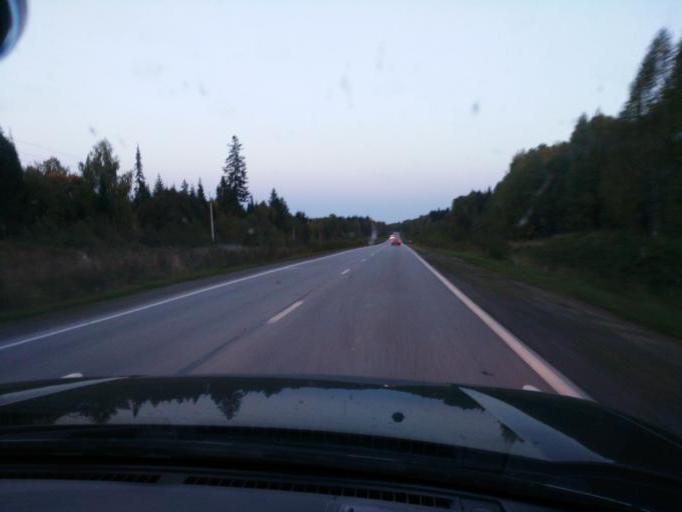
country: RU
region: Perm
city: Verkhnechusovskiye Gorodki
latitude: 58.2532
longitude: 57.0066
